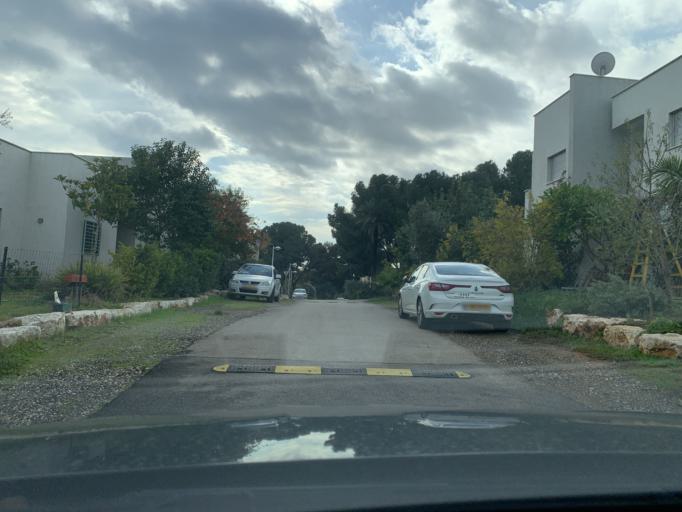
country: PS
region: West Bank
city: Qalqilyah
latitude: 32.2005
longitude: 34.9494
